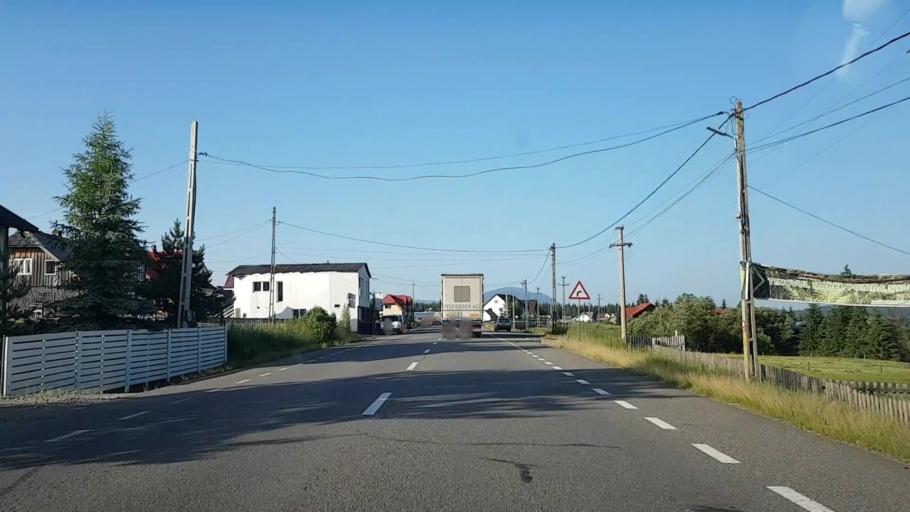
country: RO
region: Suceava
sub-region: Comuna Poiana Stampei
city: Poiana Stampei
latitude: 47.3022
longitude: 25.1099
